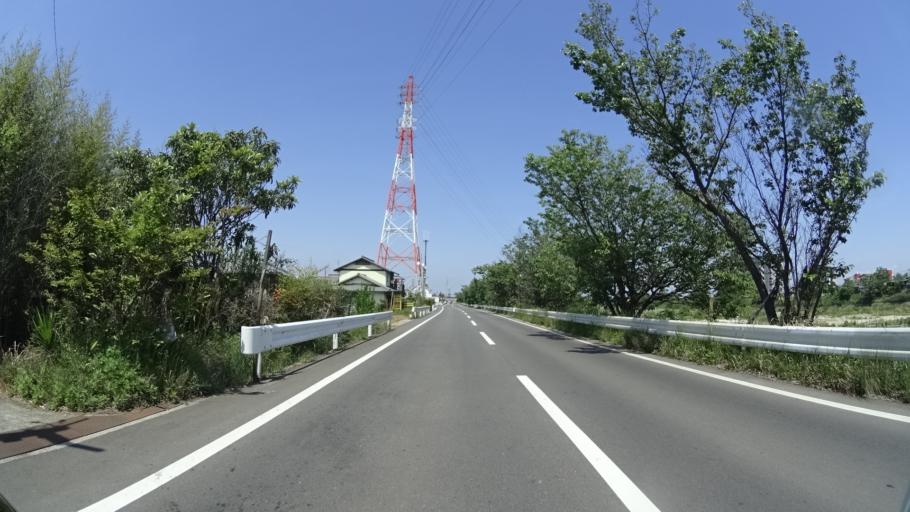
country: JP
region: Ehime
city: Hojo
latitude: 34.0433
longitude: 132.9817
